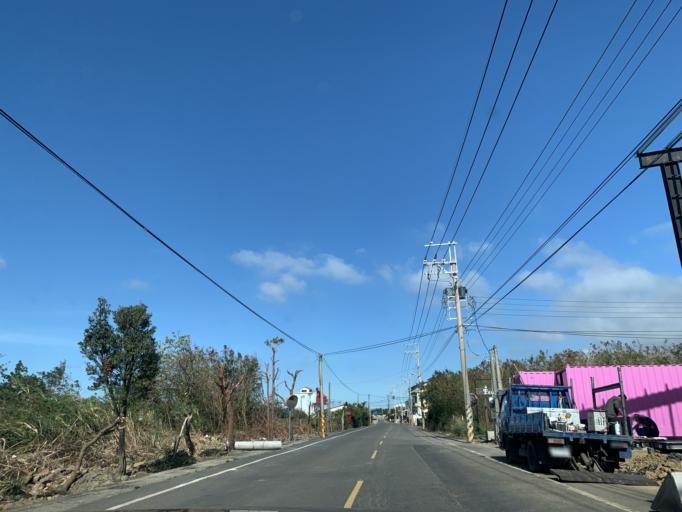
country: TW
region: Taiwan
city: Hengchun
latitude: 22.0026
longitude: 120.7524
